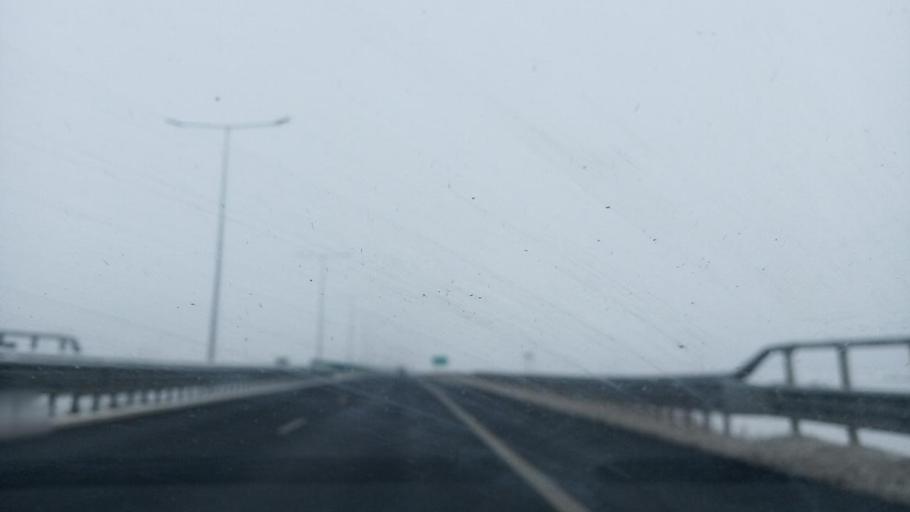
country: RO
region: Bacau
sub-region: Comuna Saucesti
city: Saucesti
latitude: 46.6025
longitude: 26.9601
